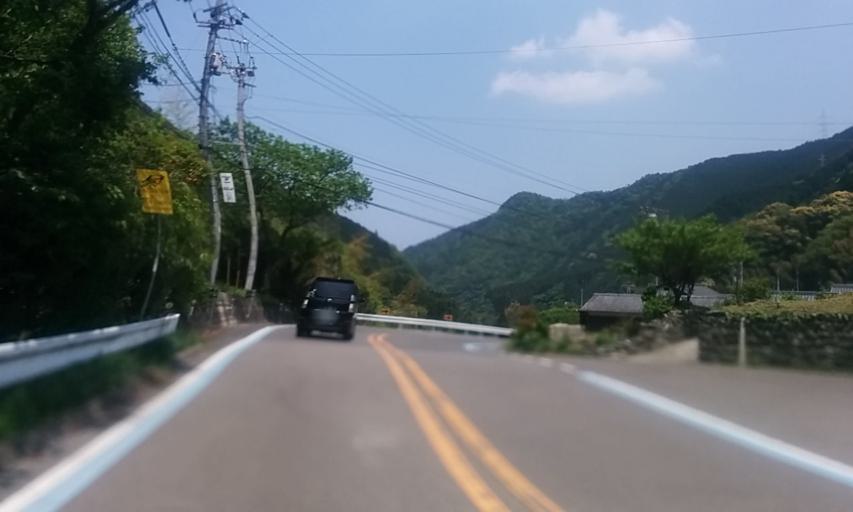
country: JP
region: Ehime
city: Niihama
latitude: 33.9085
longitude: 133.3075
